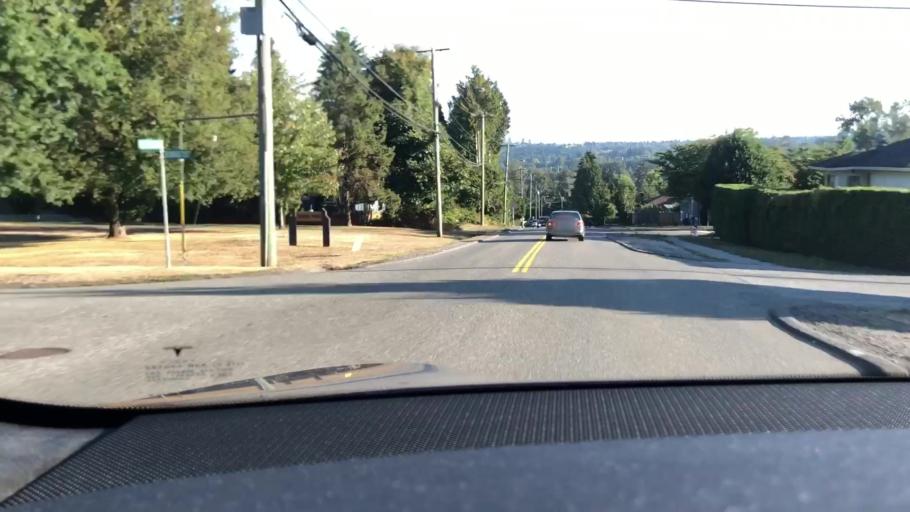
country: CA
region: British Columbia
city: Burnaby
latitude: 49.2659
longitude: -122.9702
